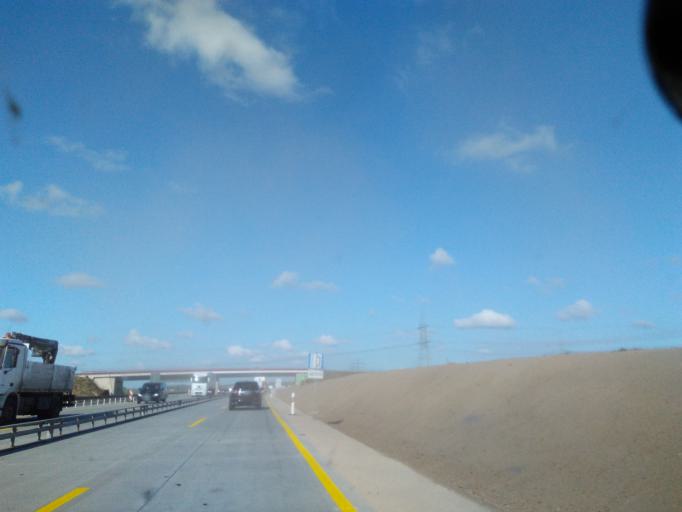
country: DE
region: Berlin
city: Buch
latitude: 52.6168
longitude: 13.5223
